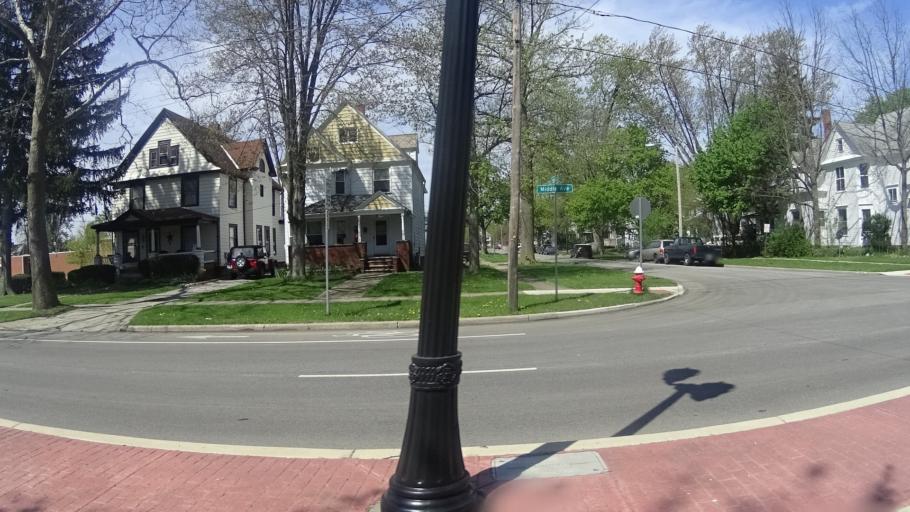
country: US
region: Ohio
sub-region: Lorain County
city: Elyria
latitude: 41.3549
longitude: -82.1073
